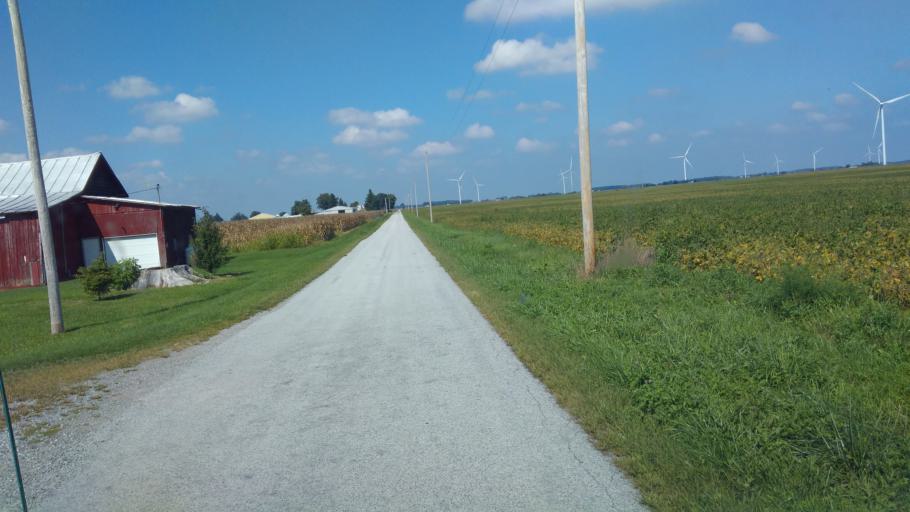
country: US
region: Ohio
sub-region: Hardin County
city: Ada
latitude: 40.7623
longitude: -83.7479
